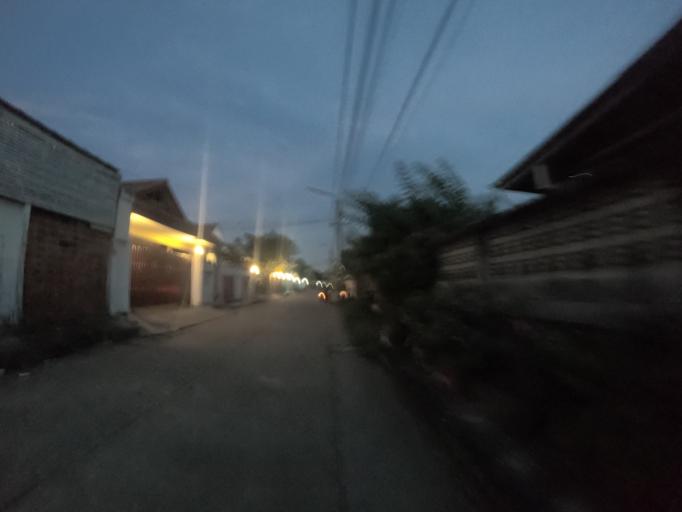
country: TH
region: Bangkok
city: Lat Phrao
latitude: 13.8263
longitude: 100.6105
